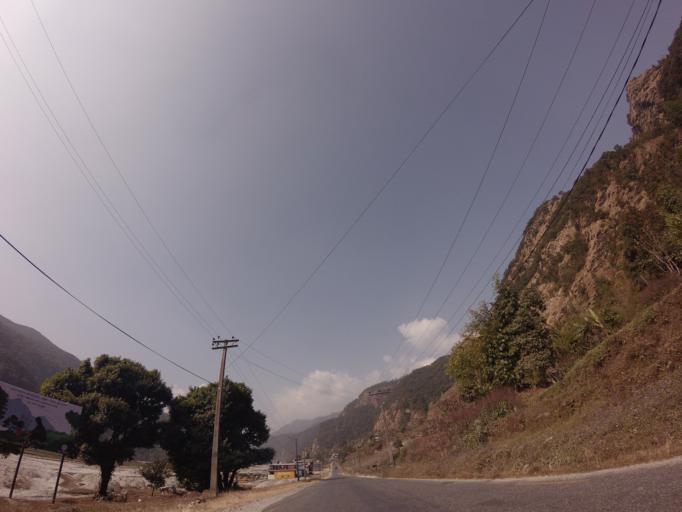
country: NP
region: Western Region
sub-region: Gandaki Zone
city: Pokhara
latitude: 28.2887
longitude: 83.8953
